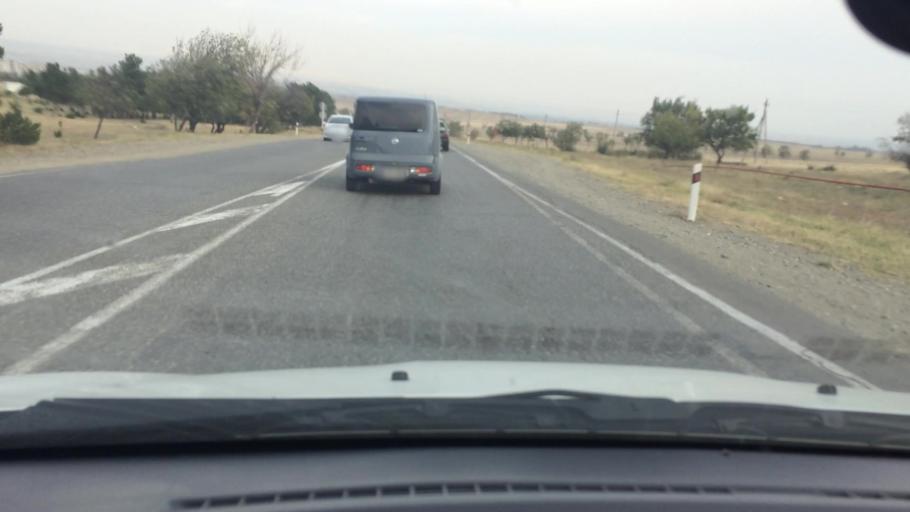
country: GE
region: T'bilisi
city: Tbilisi
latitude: 41.6390
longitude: 44.8706
